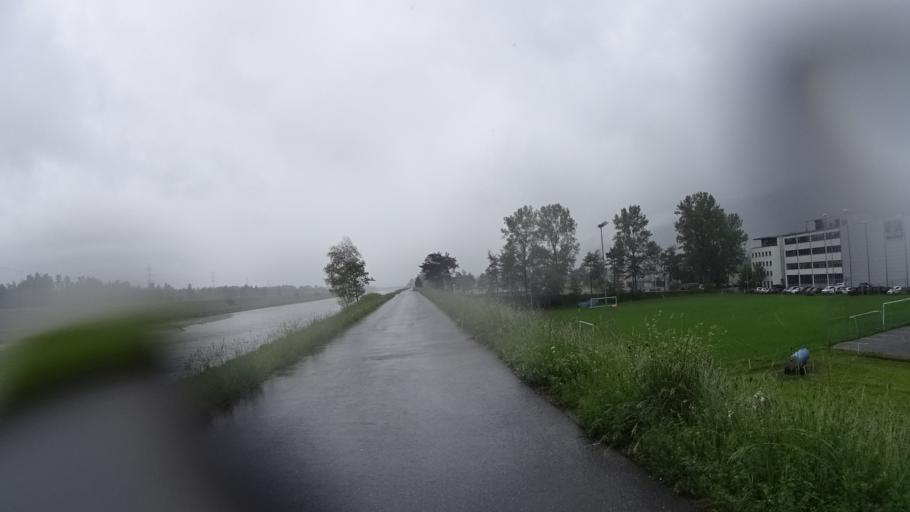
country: LI
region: Triesen
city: Triesen
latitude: 47.1079
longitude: 9.5193
